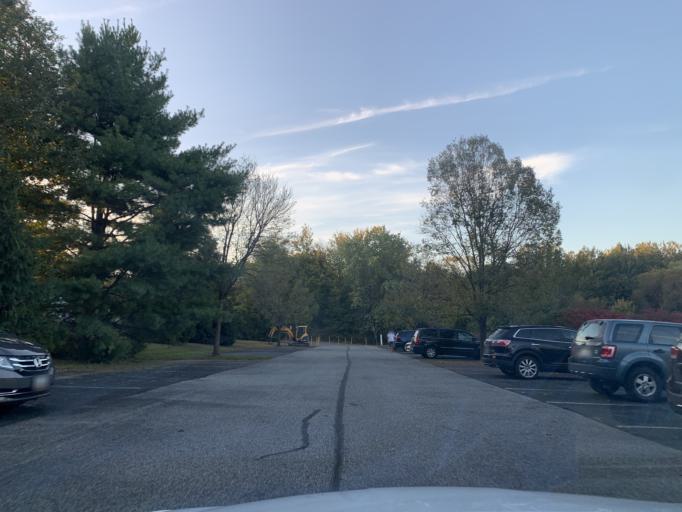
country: US
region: Maryland
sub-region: Harford County
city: South Bel Air
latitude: 39.5344
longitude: -76.3411
